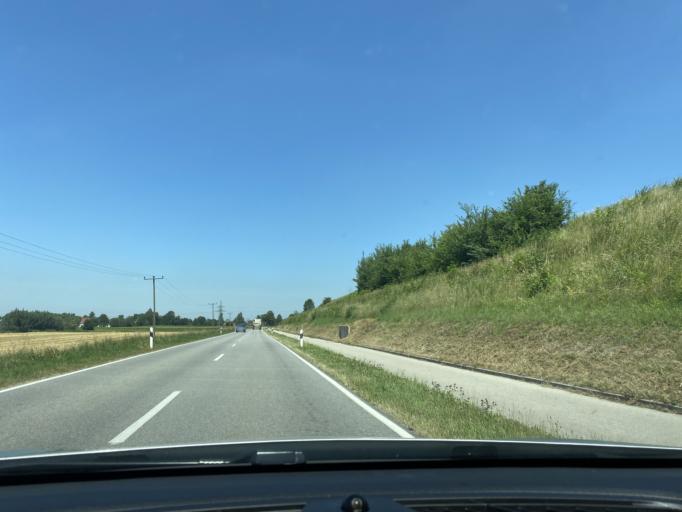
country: DE
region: Bavaria
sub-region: Upper Bavaria
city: Moosinning
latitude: 48.2621
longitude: 11.8466
